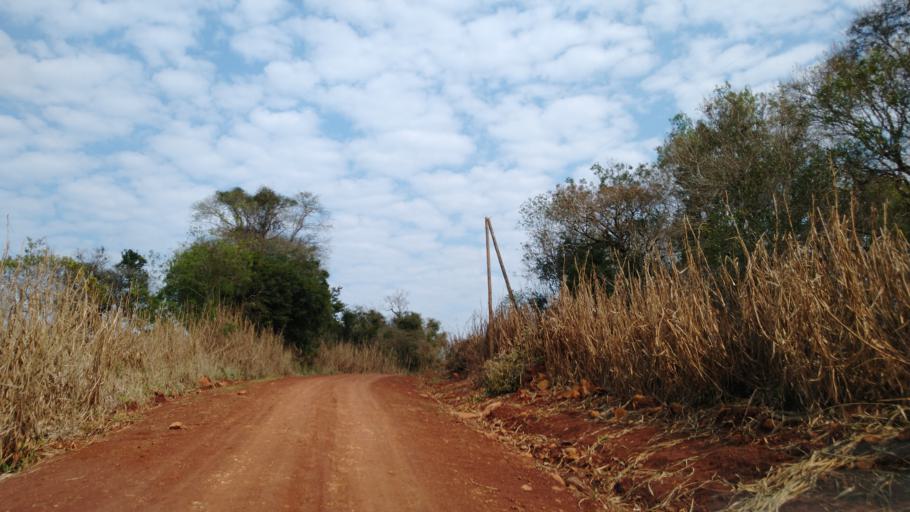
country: AR
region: Misiones
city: Capiovi
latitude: -26.9421
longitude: -55.0639
